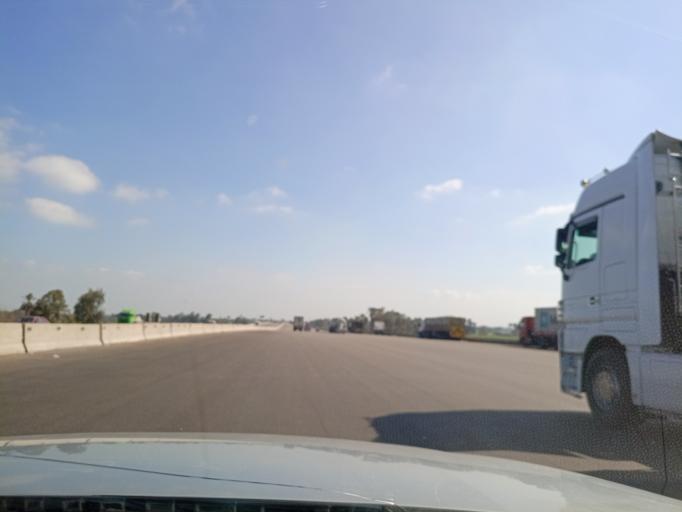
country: EG
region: Muhafazat al Qalyubiyah
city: Banha
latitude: 30.4661
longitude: 31.2999
